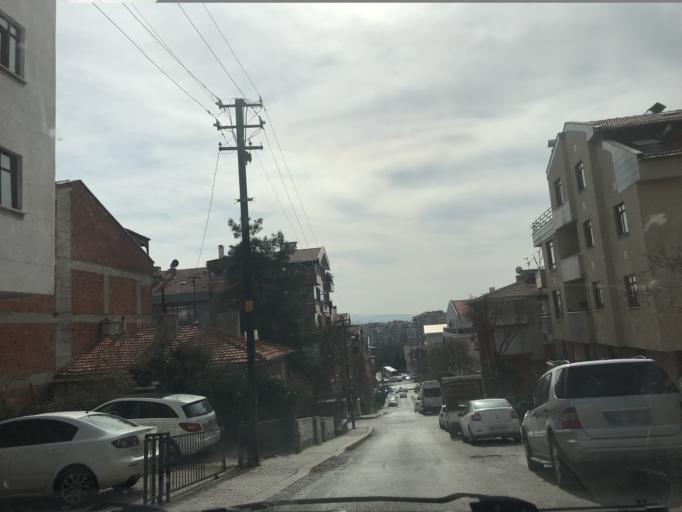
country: TR
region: Ankara
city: Batikent
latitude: 39.9658
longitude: 32.8005
